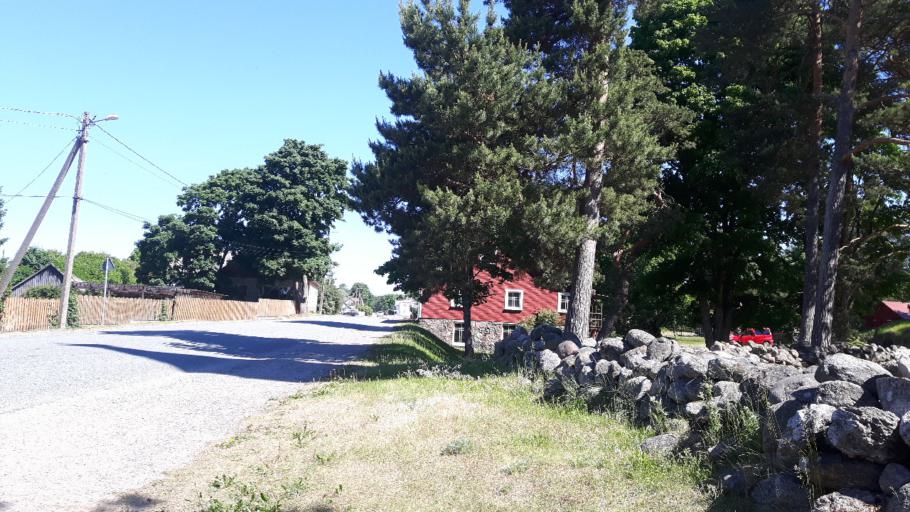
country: LV
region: Salacgrivas
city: Ainazi
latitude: 58.0797
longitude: 24.4989
